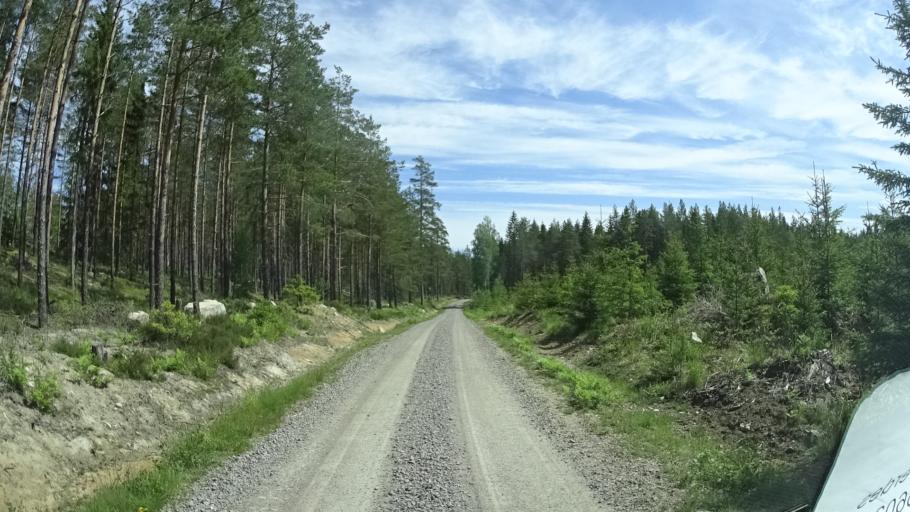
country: SE
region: OEstergoetland
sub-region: Norrkopings Kommun
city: Svartinge
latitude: 58.7713
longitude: 15.9345
